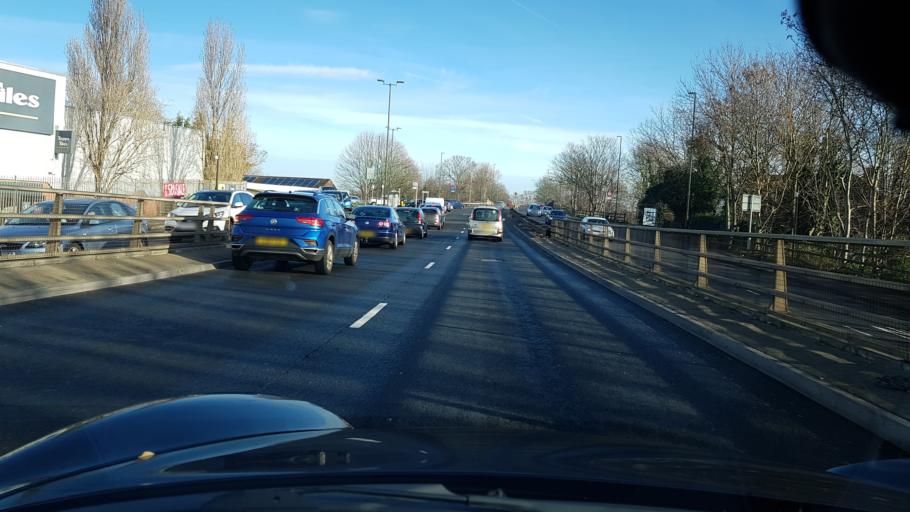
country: GB
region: England
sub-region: Greater London
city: New Malden
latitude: 51.4044
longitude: -0.2381
